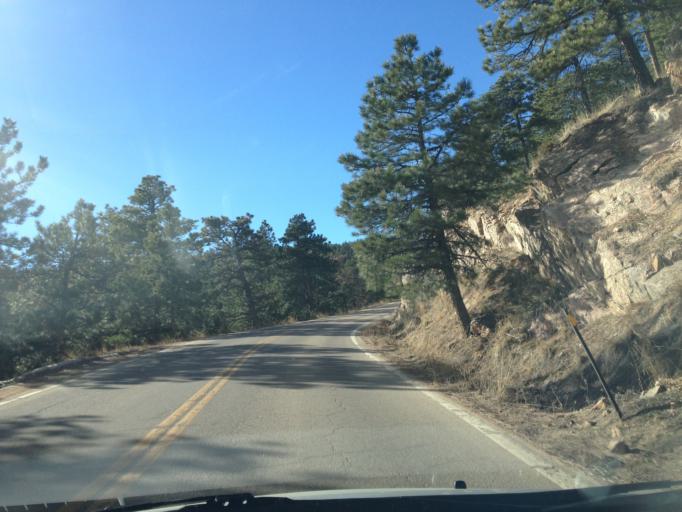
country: US
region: Colorado
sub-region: Boulder County
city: Boulder
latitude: 39.9931
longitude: -105.3116
